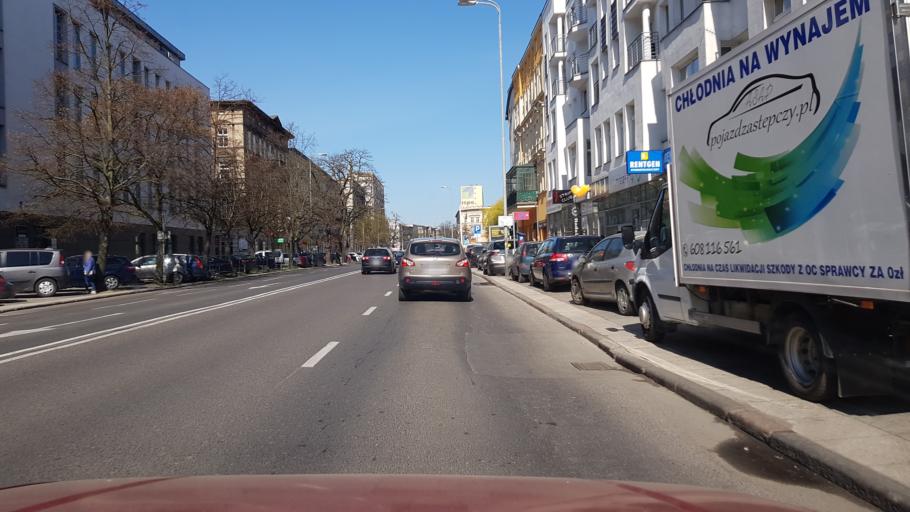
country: PL
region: West Pomeranian Voivodeship
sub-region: Szczecin
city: Szczecin
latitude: 53.4267
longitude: 14.5458
